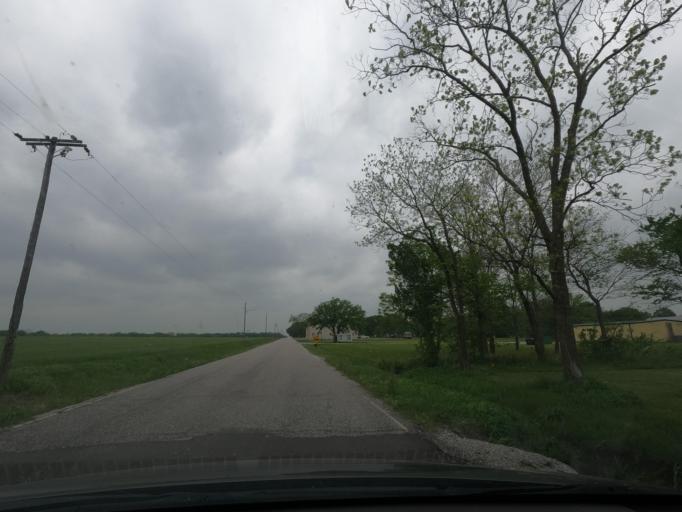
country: US
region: Kansas
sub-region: Cherokee County
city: Columbus
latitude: 37.2817
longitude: -94.9236
